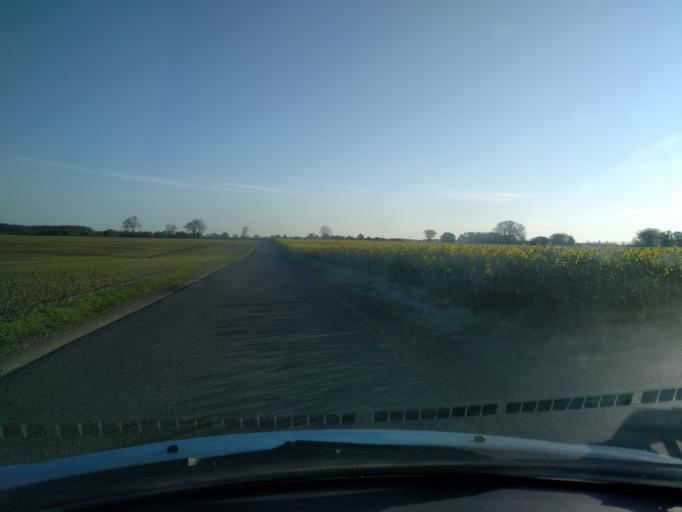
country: DK
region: South Denmark
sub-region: Kerteminde Kommune
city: Langeskov
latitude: 55.4067
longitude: 10.5611
